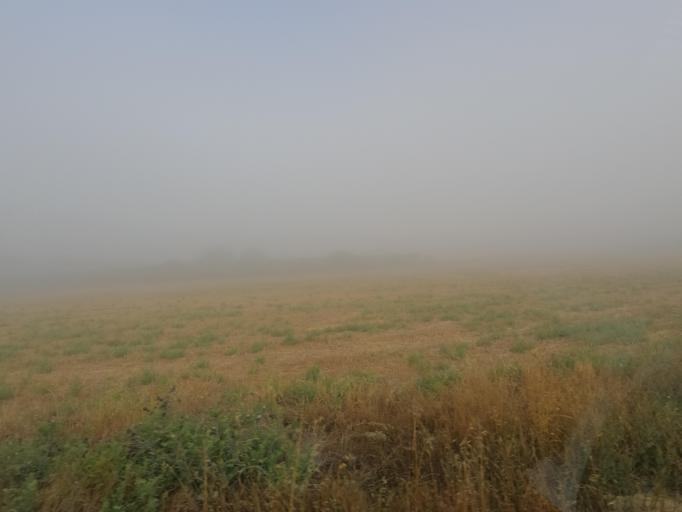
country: CY
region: Ammochostos
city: Acheritou
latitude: 35.0890
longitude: 33.8760
